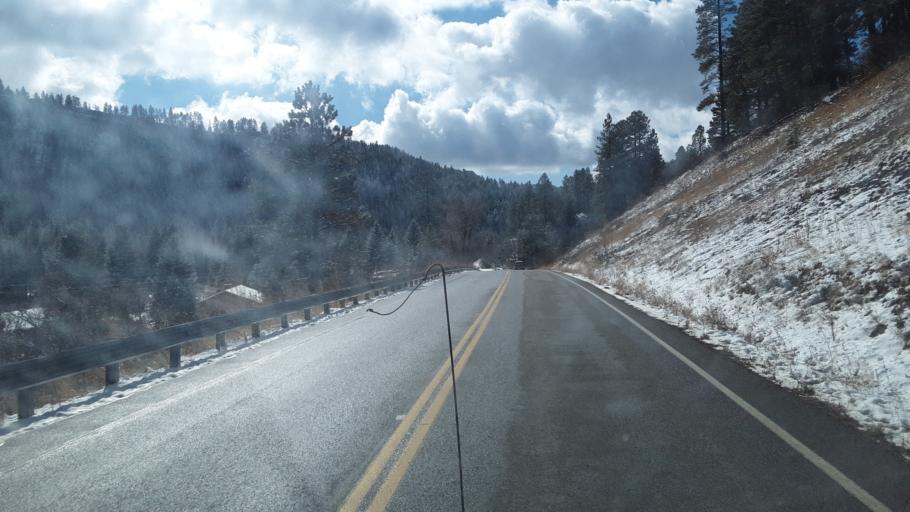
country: US
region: Colorado
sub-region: La Plata County
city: Bayfield
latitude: 37.3496
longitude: -107.6959
